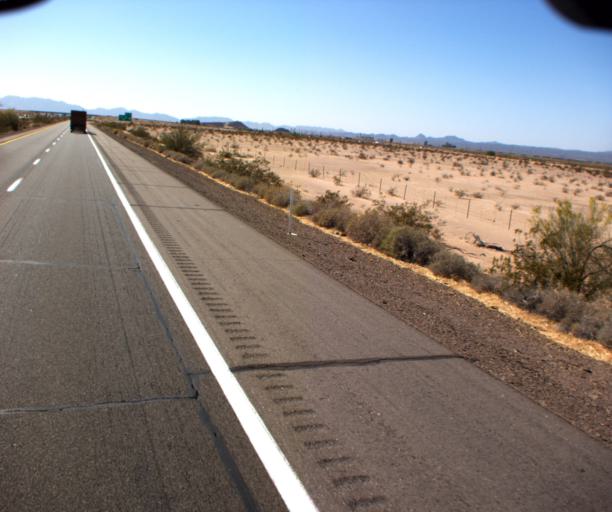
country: US
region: Arizona
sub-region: Yuma County
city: Wellton
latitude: 32.6836
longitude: -114.0130
